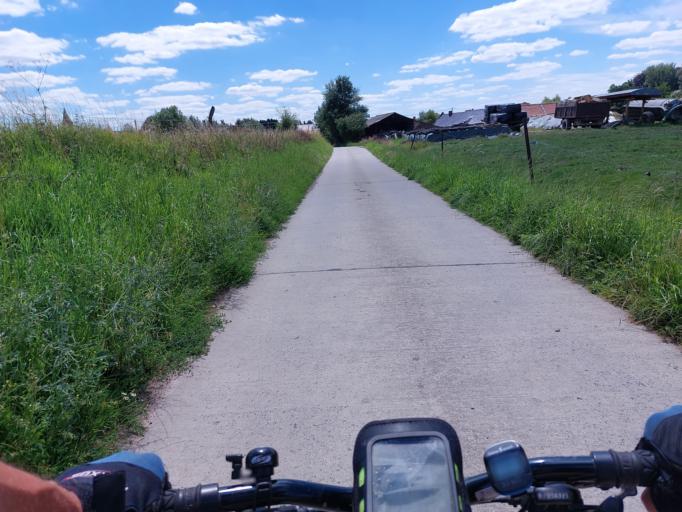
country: BE
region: Wallonia
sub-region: Province du Hainaut
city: Brugelette
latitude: 50.6099
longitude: 3.8917
